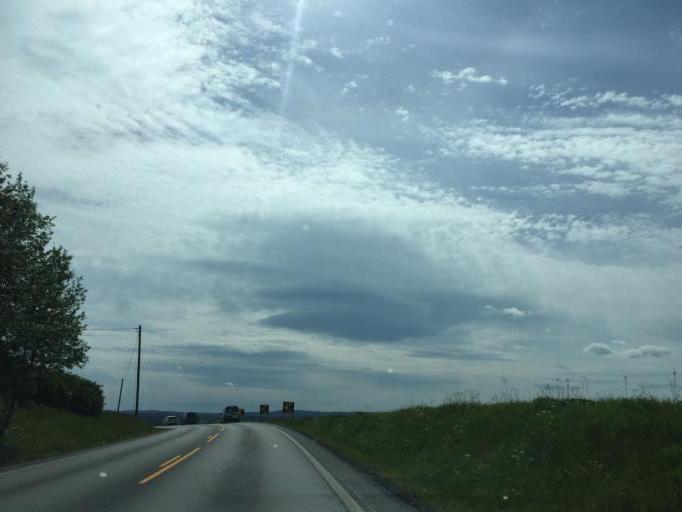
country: NO
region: Akershus
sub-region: Nes
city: Arnes
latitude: 60.1302
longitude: 11.4413
